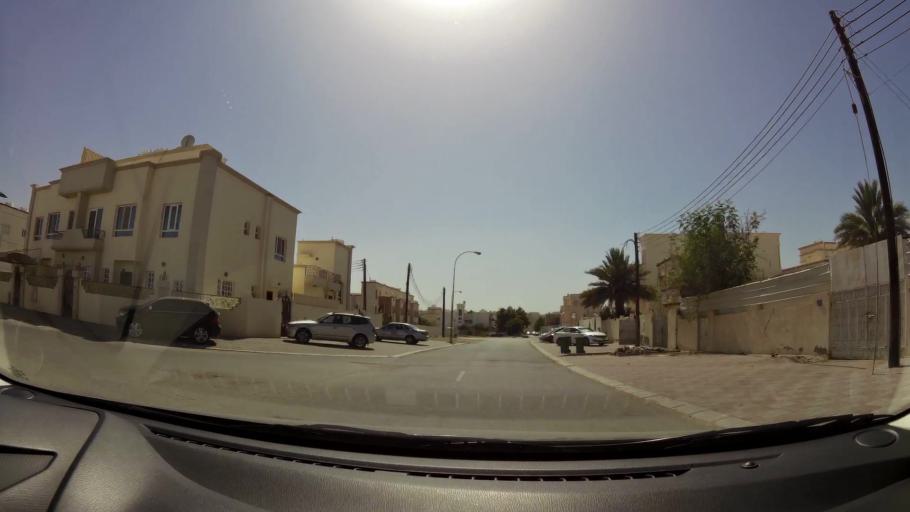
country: OM
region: Muhafazat Masqat
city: Bawshar
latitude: 23.6011
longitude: 58.3799
